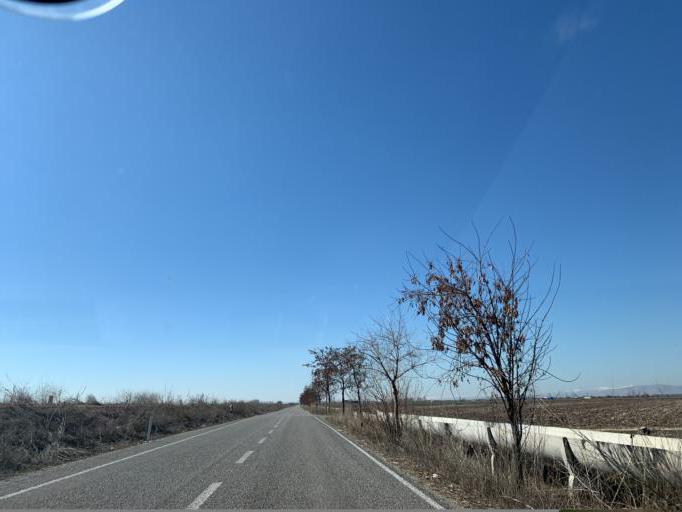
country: TR
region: Konya
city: Catalhoeyuek
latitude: 37.6242
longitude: 32.8045
